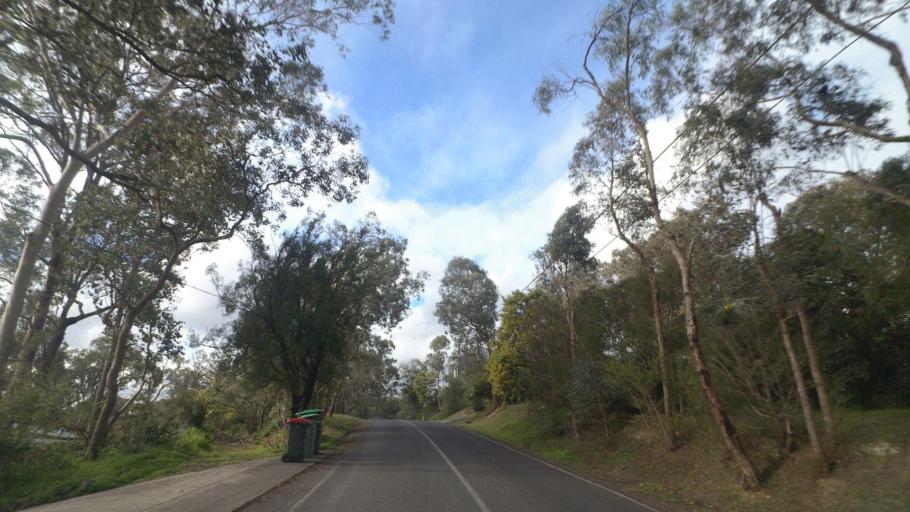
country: AU
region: Victoria
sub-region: Nillumbik
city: North Warrandyte
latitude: -37.7366
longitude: 145.2144
